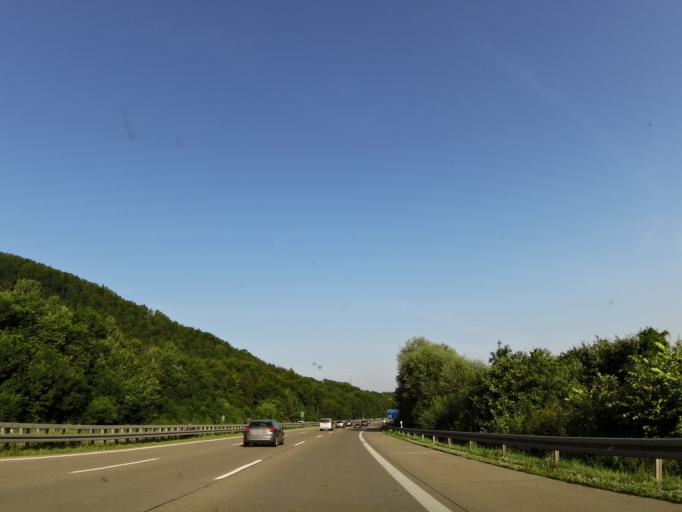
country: DE
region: Baden-Wuerttemberg
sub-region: Regierungsbezirk Stuttgart
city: Boll
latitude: 48.6148
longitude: 9.6054
